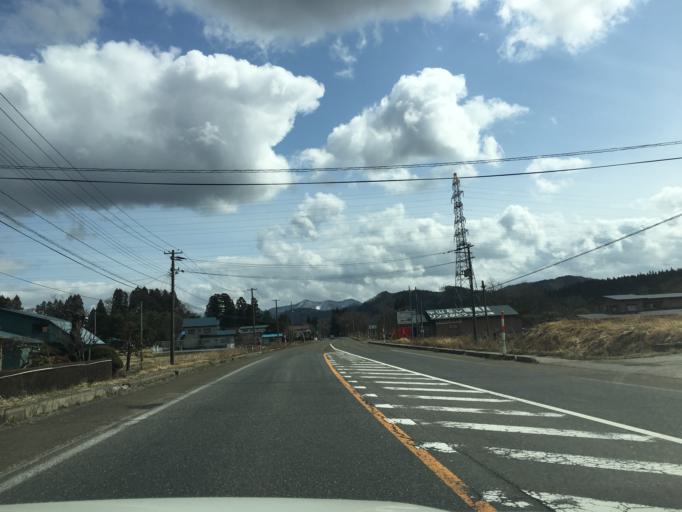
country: JP
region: Akita
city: Odate
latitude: 40.2275
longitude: 140.5991
